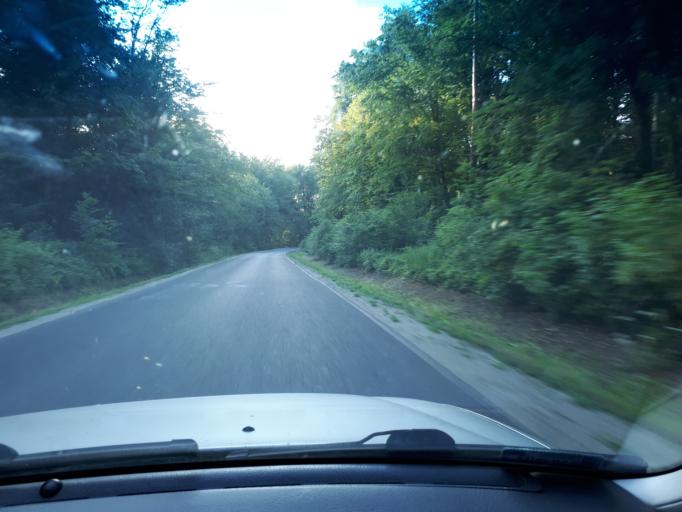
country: PL
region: Subcarpathian Voivodeship
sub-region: Powiat debicki
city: Debica
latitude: 49.9779
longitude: 21.4100
